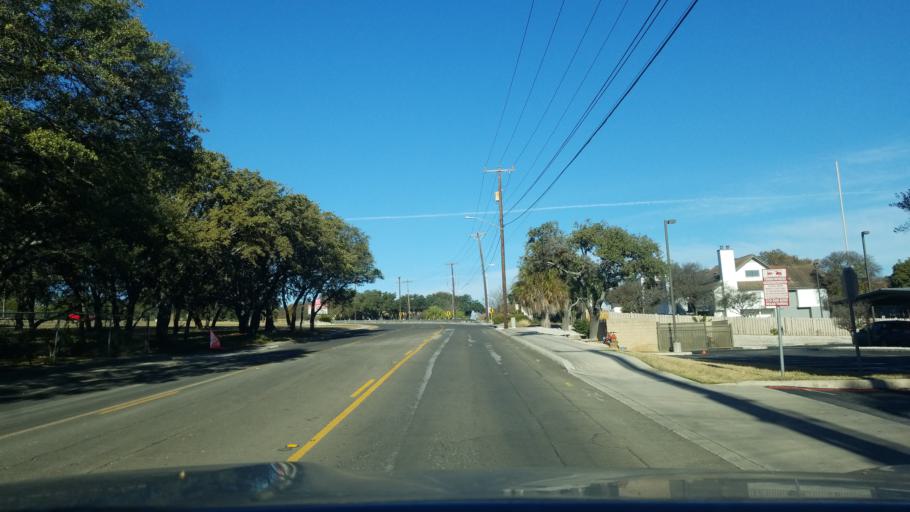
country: US
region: Texas
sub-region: Bexar County
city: Balcones Heights
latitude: 29.5322
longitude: -98.5663
